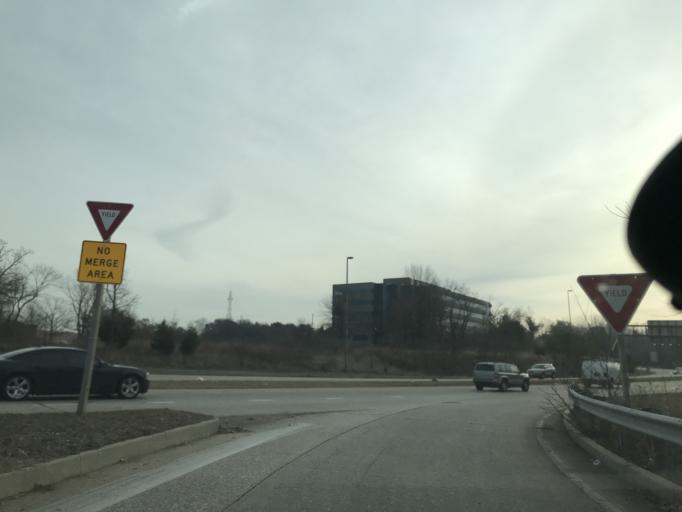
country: US
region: Maryland
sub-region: Prince George's County
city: Springdale
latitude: 38.9488
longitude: -76.8404
